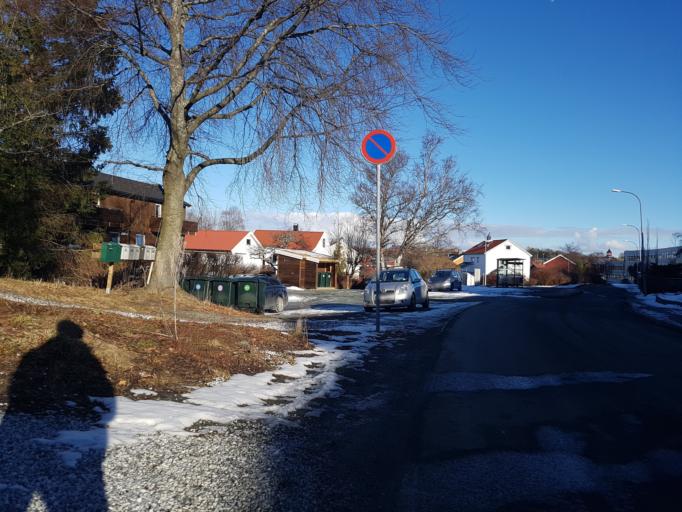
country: NO
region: Sor-Trondelag
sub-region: Trondheim
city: Trondheim
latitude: 63.4479
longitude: 10.4309
